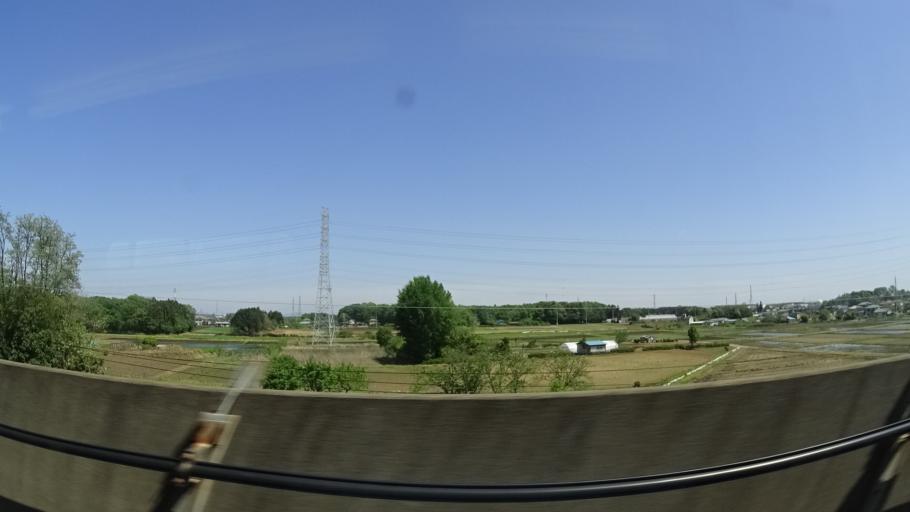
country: JP
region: Tochigi
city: Mibu
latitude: 36.3619
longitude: 139.8348
